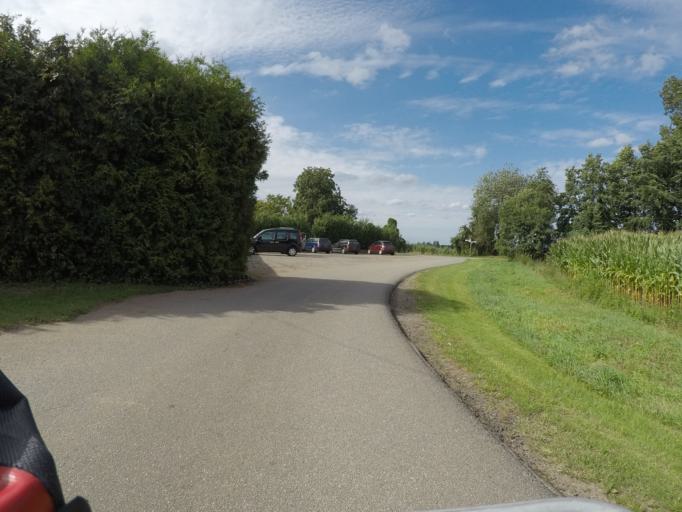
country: DE
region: Lower Saxony
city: Wittorf
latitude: 53.3512
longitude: 10.3754
